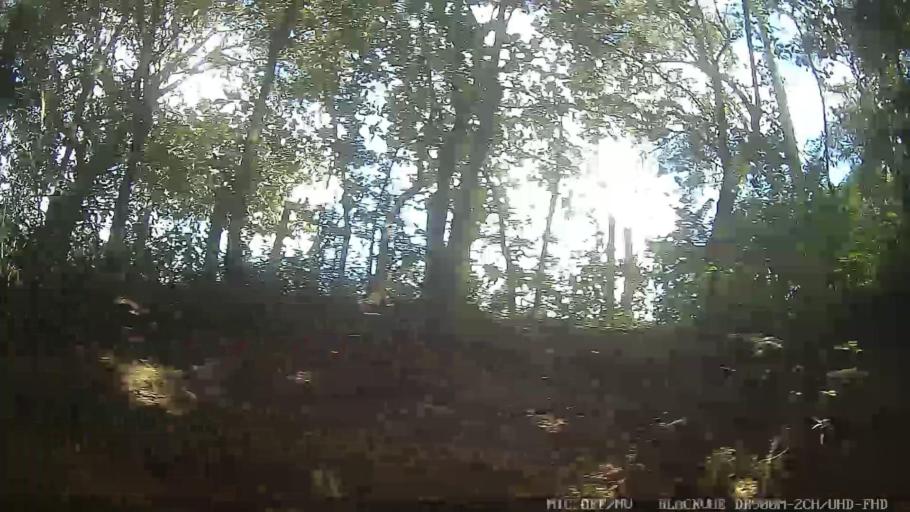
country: BR
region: Sao Paulo
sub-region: Bom Jesus Dos Perdoes
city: Bom Jesus dos Perdoes
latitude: -23.1362
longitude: -46.5054
